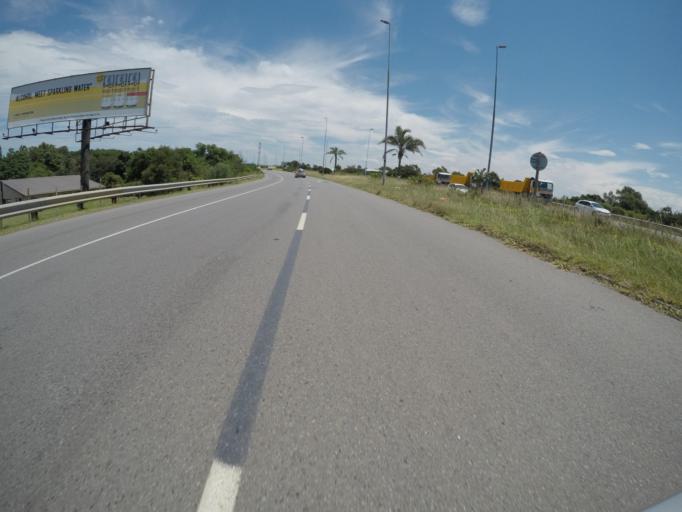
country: ZA
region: Eastern Cape
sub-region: Buffalo City Metropolitan Municipality
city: East London
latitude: -33.0368
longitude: 27.8345
